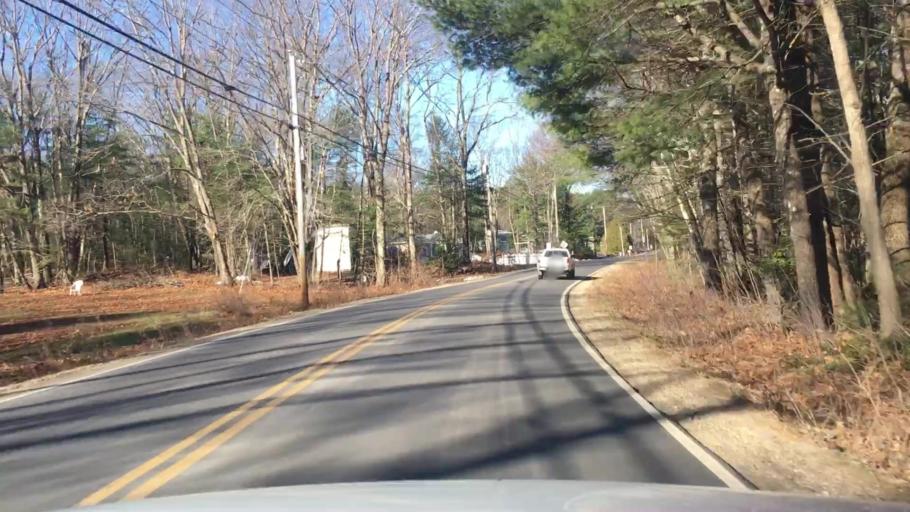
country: US
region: Maine
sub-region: York County
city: Arundel
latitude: 43.4132
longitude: -70.4984
